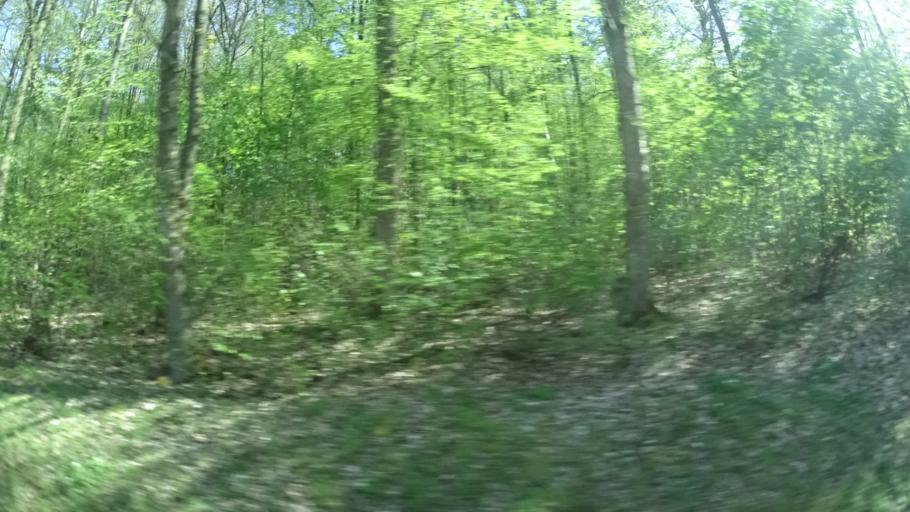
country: DE
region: Bavaria
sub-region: Regierungsbezirk Unterfranken
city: Hofheim in Unterfranken
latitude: 50.1349
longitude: 10.5802
